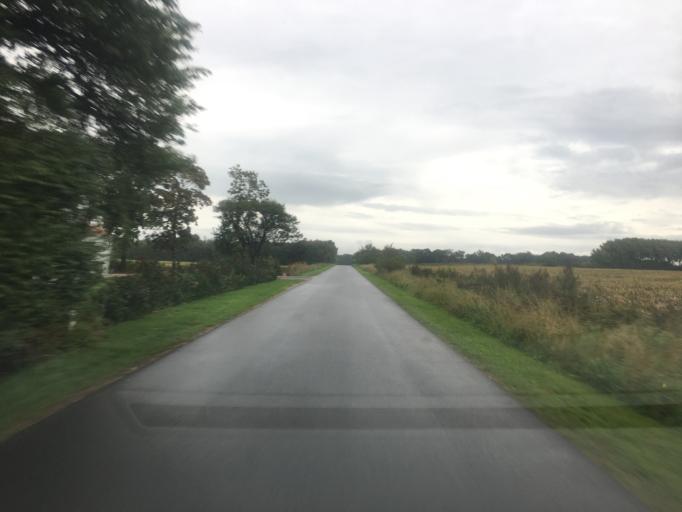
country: DK
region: South Denmark
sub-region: Tonder Kommune
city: Logumkloster
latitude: 54.9906
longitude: 8.9722
